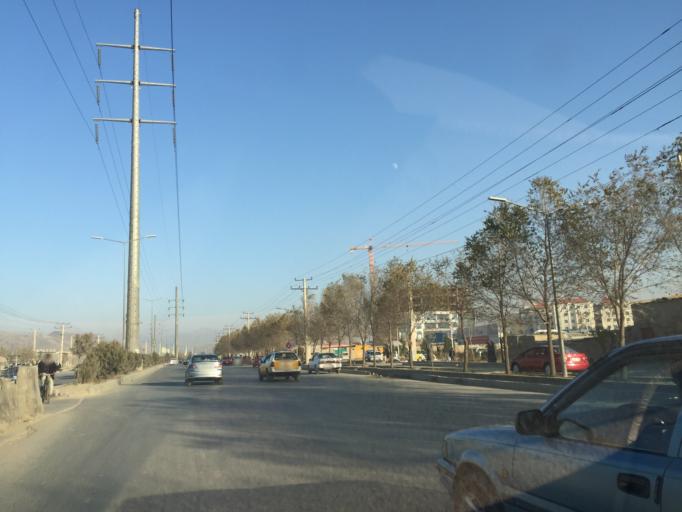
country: AF
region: Kabul
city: Kabul
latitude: 34.5672
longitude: 69.1771
